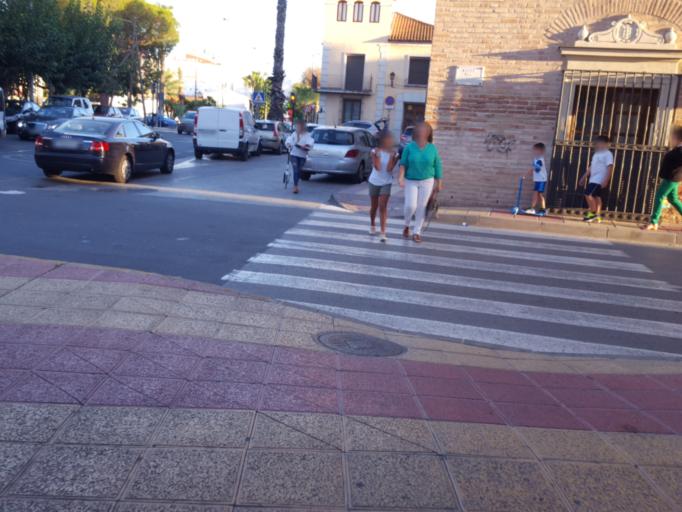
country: ES
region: Murcia
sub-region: Murcia
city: Murcia
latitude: 38.0079
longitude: -1.1513
